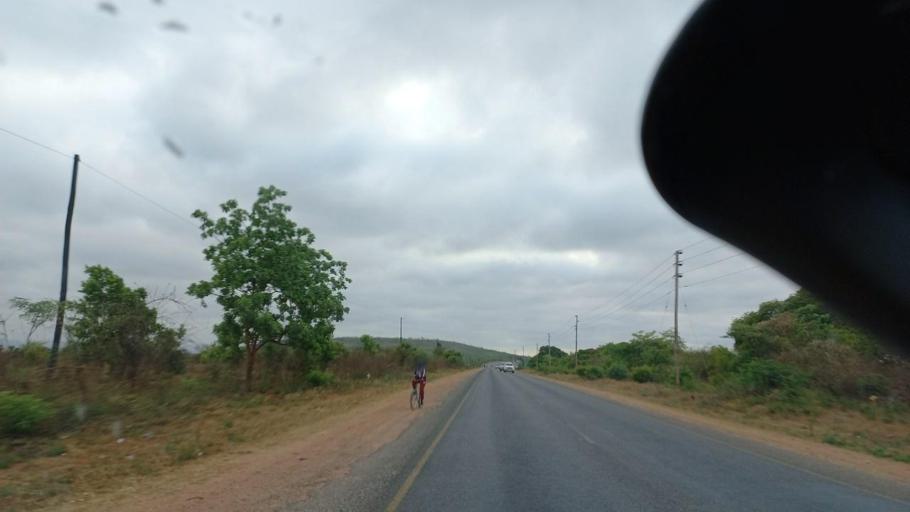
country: ZM
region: Lusaka
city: Chongwe
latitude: -15.3450
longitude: 28.5867
